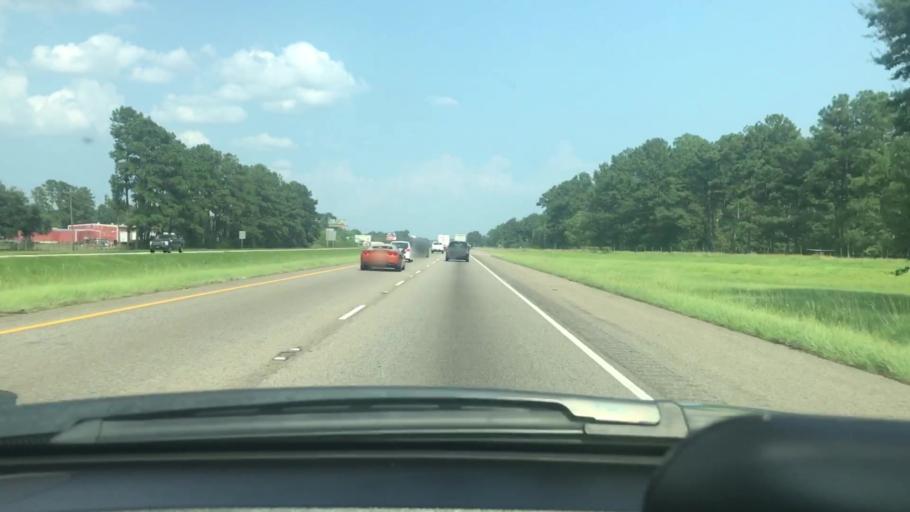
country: US
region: Louisiana
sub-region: Livingston Parish
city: Albany
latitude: 30.4746
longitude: -90.6398
